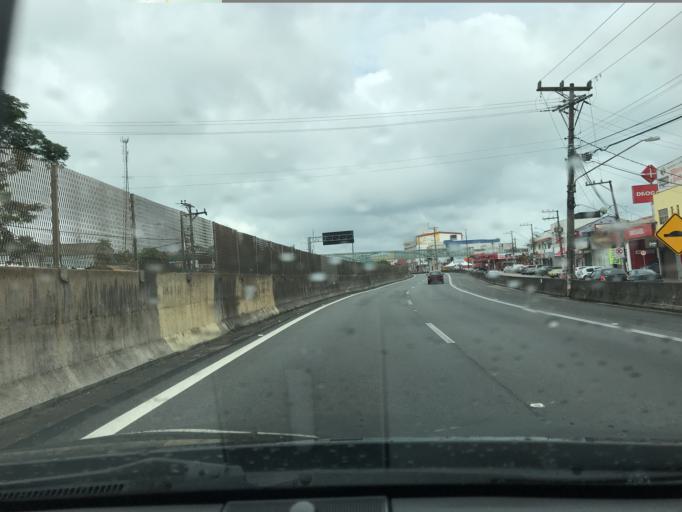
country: BR
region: Sao Paulo
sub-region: Vargem Grande Paulista
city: Vargem Grande Paulista
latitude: -23.6054
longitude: -47.0220
